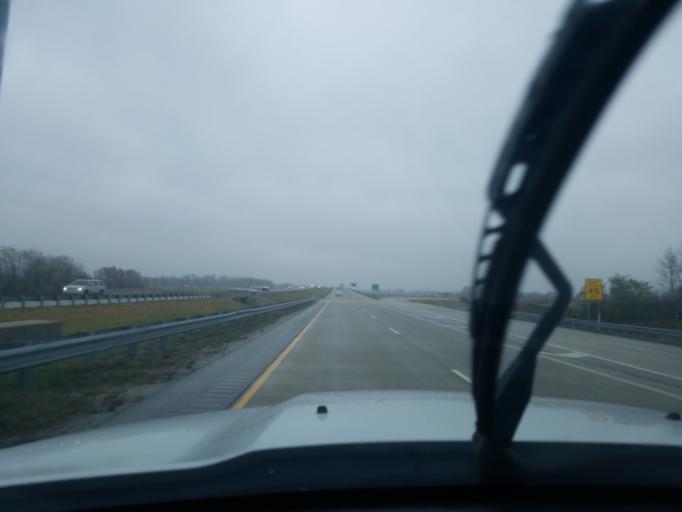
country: US
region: Indiana
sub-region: Howard County
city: Kokomo
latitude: 40.4828
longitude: -86.0856
